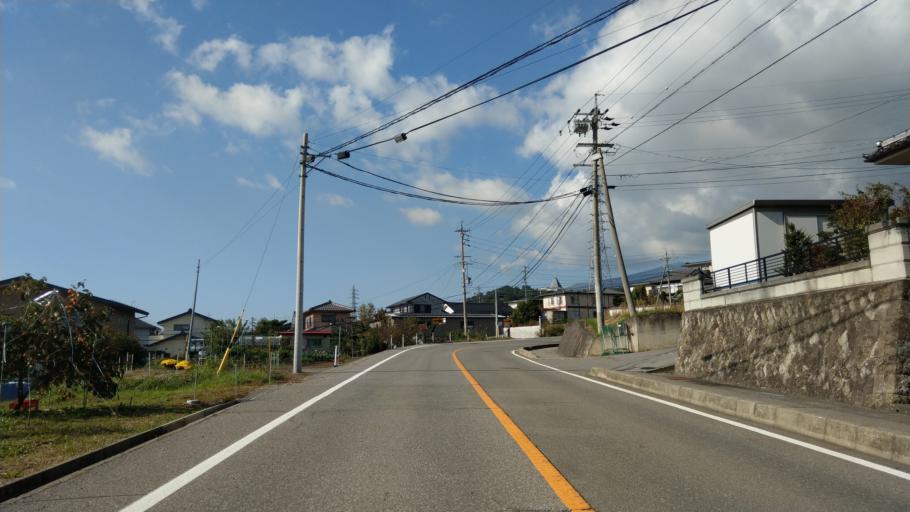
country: JP
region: Nagano
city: Komoro
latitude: 36.3338
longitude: 138.4266
